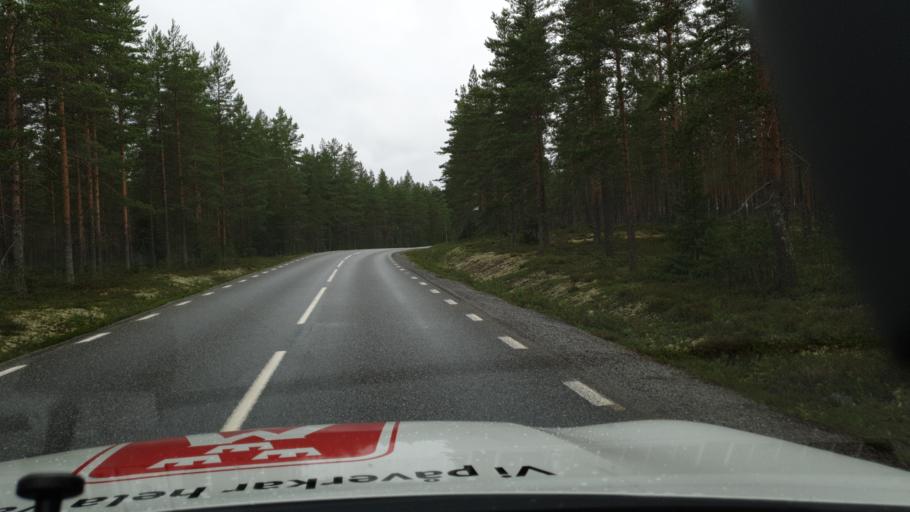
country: SE
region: Vaesterbotten
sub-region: Umea Kommun
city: Saevar
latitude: 63.9940
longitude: 20.4953
